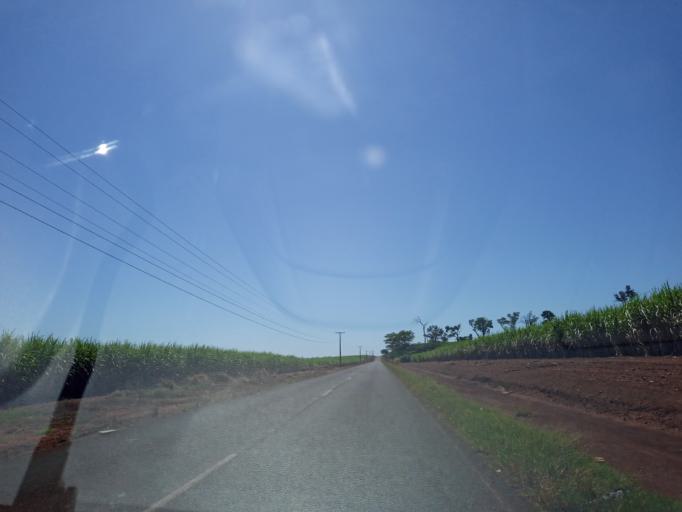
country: BR
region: Goias
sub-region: Itumbiara
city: Itumbiara
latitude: -18.4259
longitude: -49.1759
